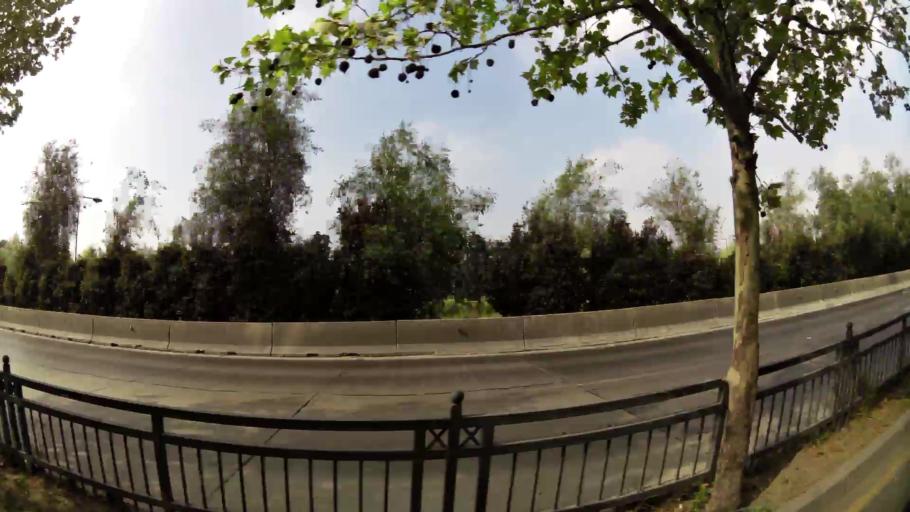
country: CL
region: Santiago Metropolitan
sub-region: Provincia de Santiago
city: Villa Presidente Frei, Nunoa, Santiago, Chile
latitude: -33.3848
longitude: -70.5366
